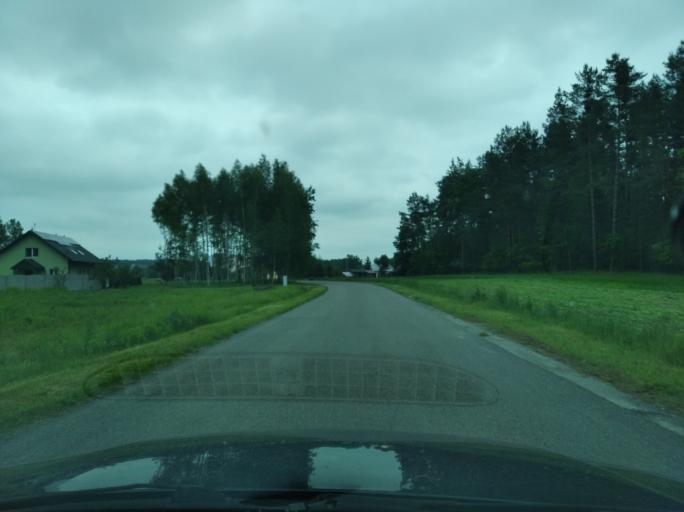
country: PL
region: Subcarpathian Voivodeship
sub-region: Powiat kolbuszowski
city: Niwiska
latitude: 50.2129
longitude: 21.6666
